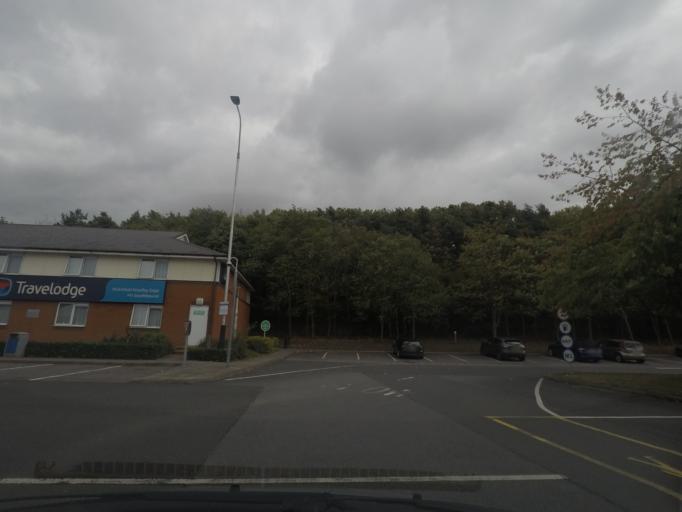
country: GB
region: England
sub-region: City and Borough of Wakefield
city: Crigglestone
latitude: 53.6216
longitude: -1.5456
